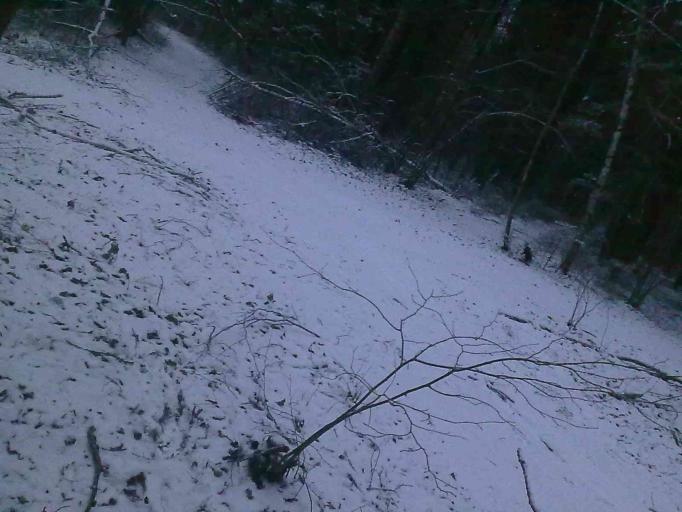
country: RU
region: Moskovskaya
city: Zhavoronki
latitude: 55.6689
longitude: 37.1183
